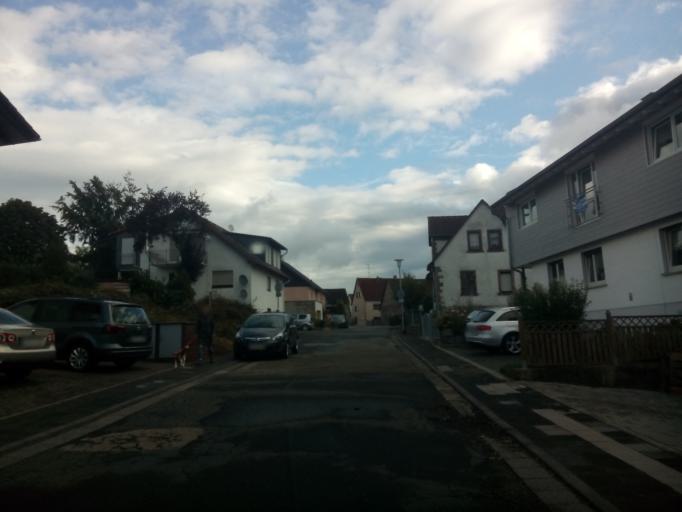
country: DE
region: Hesse
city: Gross-Umstadt
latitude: 49.8186
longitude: 8.9150
